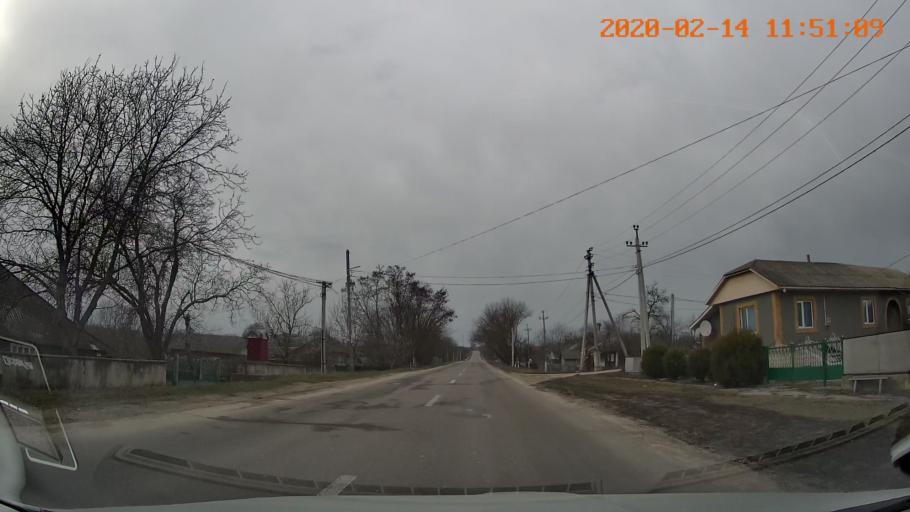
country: RO
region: Botosani
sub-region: Comuna Radauti-Prut
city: Miorcani
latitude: 48.2914
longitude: 26.9207
